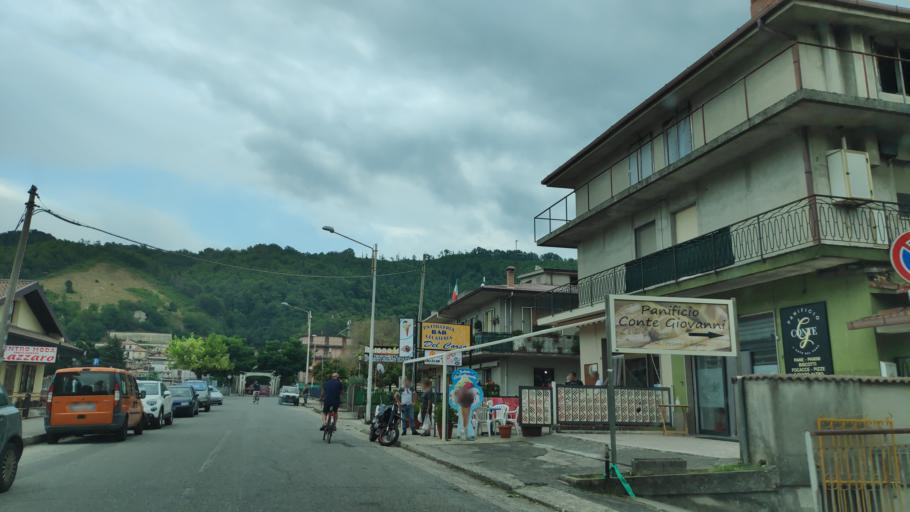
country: IT
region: Calabria
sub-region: Provincia di Catanzaro
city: Cardinale
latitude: 38.6447
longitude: 16.3850
